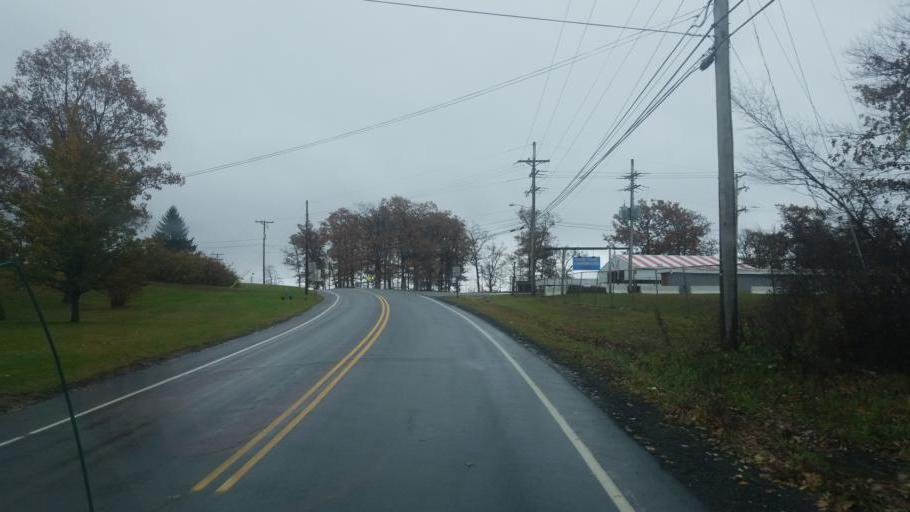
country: US
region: Pennsylvania
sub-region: Centre County
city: Milesburg
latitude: 41.0262
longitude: -77.9453
